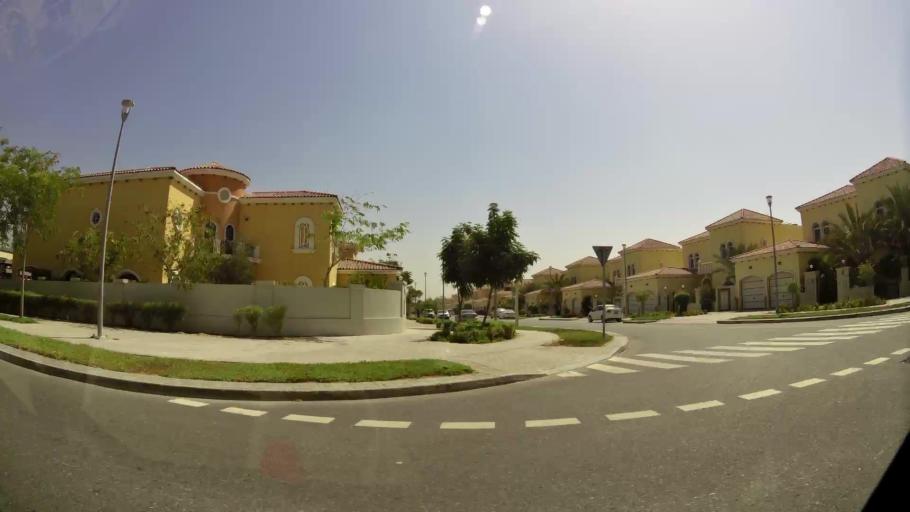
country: AE
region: Dubai
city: Dubai
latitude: 25.0525
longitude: 55.1438
